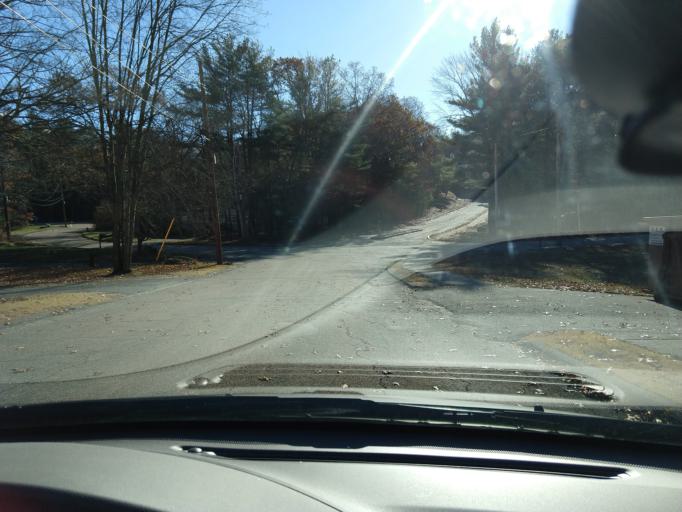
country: US
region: Massachusetts
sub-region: Middlesex County
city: Pinehurst
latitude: 42.4977
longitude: -71.2416
